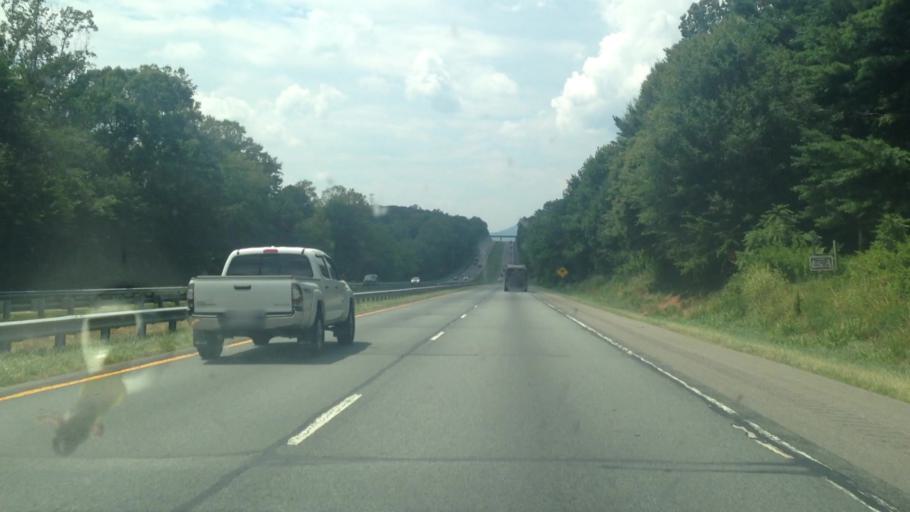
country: US
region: North Carolina
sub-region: Stokes County
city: King
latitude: 36.2773
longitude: -80.3825
